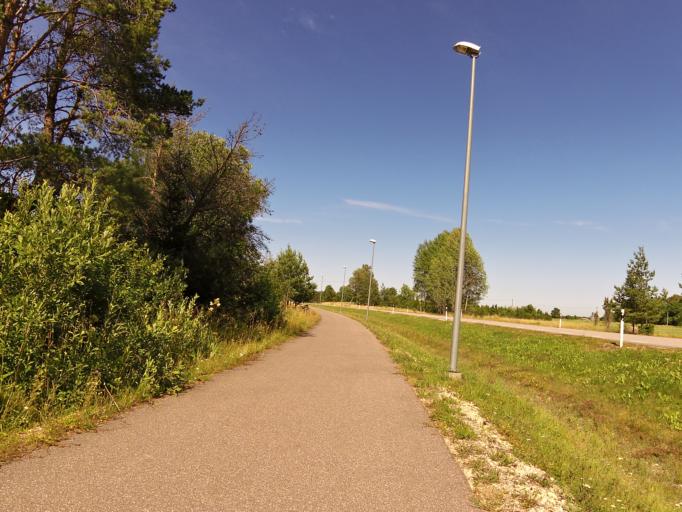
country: EE
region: Hiiumaa
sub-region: Kaerdla linn
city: Kardla
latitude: 58.9808
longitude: 22.5095
